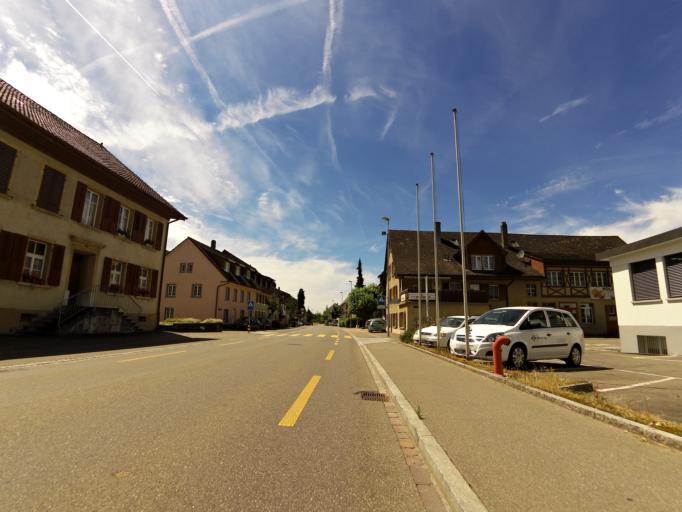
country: CH
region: Aargau
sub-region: Bezirk Rheinfelden
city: Stein
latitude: 47.5425
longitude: 7.9506
